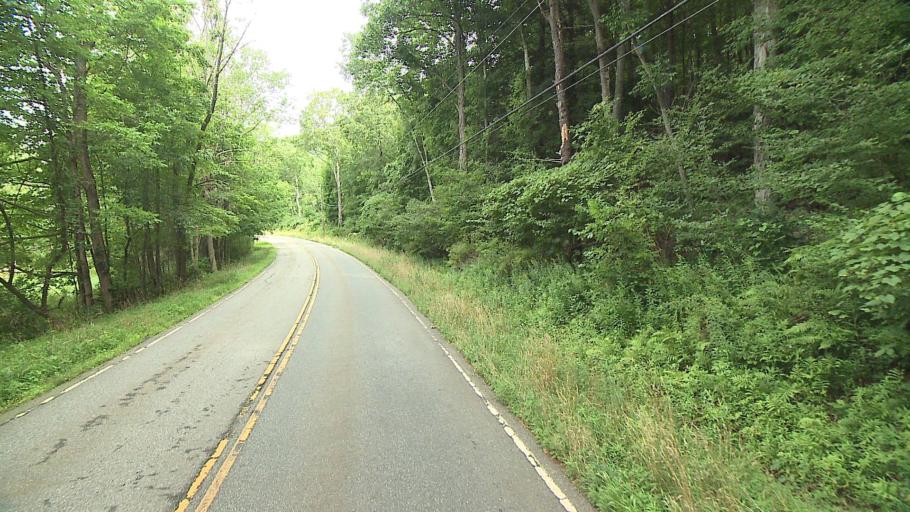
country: US
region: Connecticut
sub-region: Litchfield County
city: Kent
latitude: 41.7510
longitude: -73.5082
